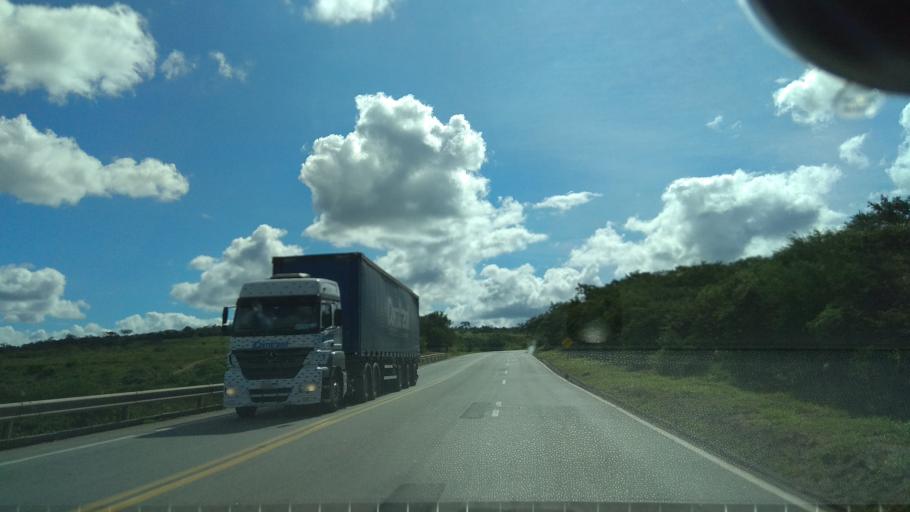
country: BR
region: Bahia
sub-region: Santa Ines
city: Santa Ines
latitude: -13.2221
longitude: -40.0271
